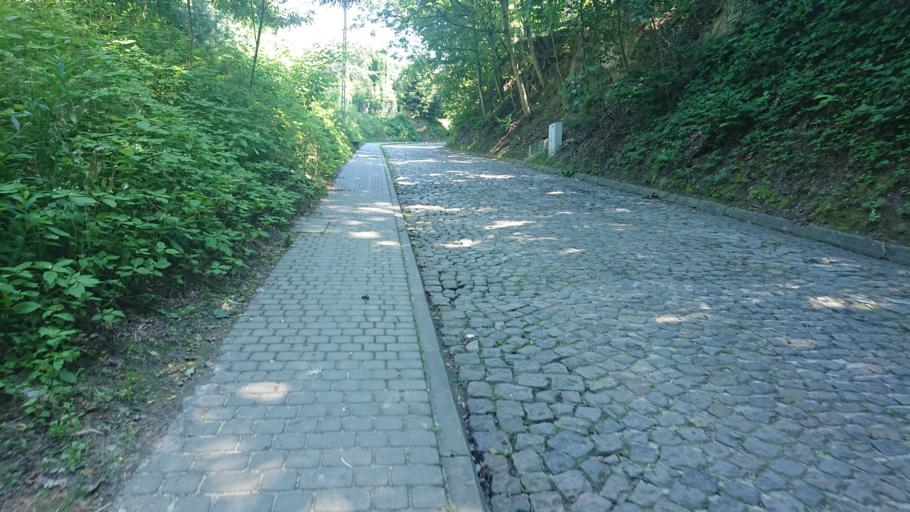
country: PL
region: Lublin Voivodeship
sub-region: Powiat pulawski
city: Kazimierz Dolny
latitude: 51.3244
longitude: 21.9539
